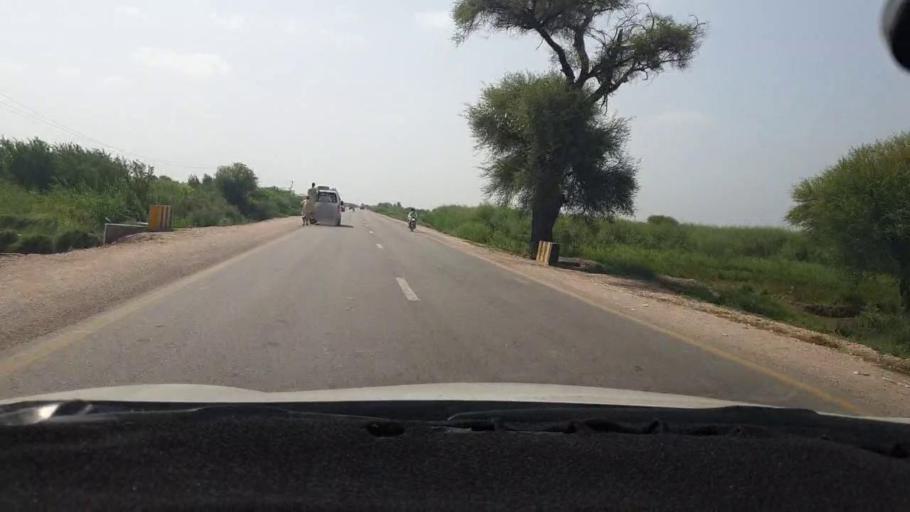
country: PK
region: Sindh
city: Mirpur Khas
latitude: 25.6034
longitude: 69.0834
